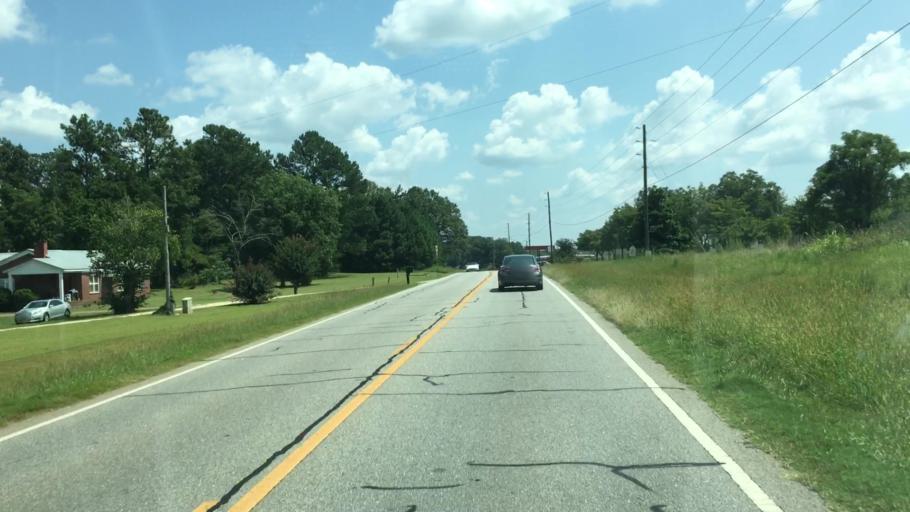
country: US
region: Georgia
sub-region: Barrow County
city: Statham
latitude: 33.9455
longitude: -83.6469
